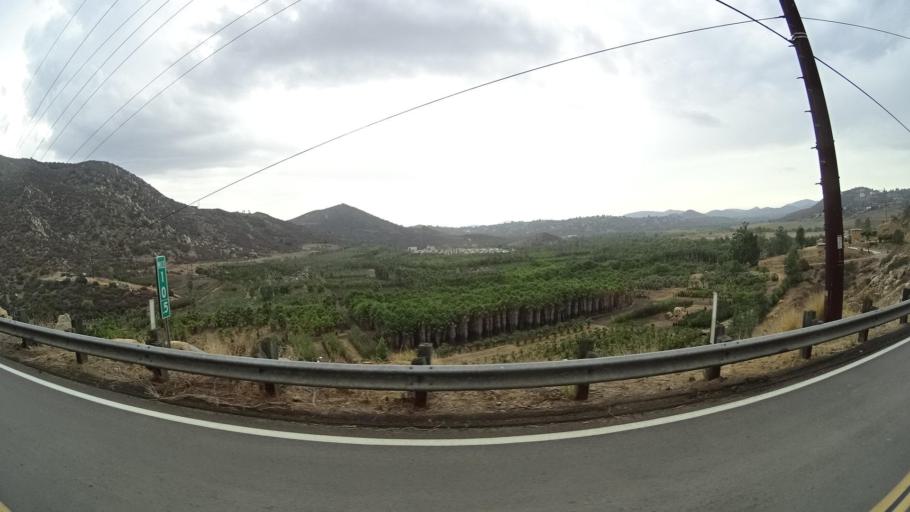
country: US
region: California
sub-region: San Diego County
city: San Pasqual
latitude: 33.0629
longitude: -117.0249
